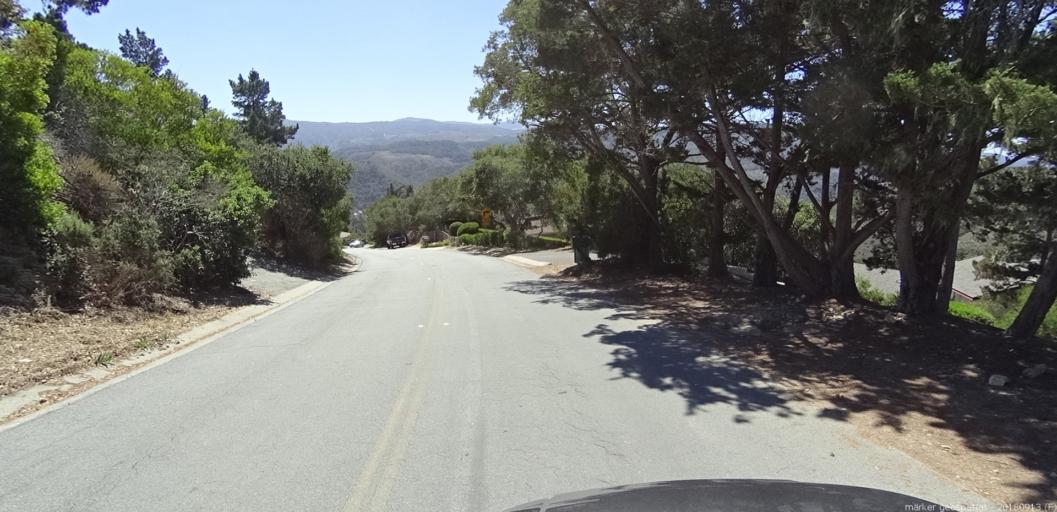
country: US
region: California
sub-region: Monterey County
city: Carmel Valley Village
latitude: 36.5286
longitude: -121.8036
